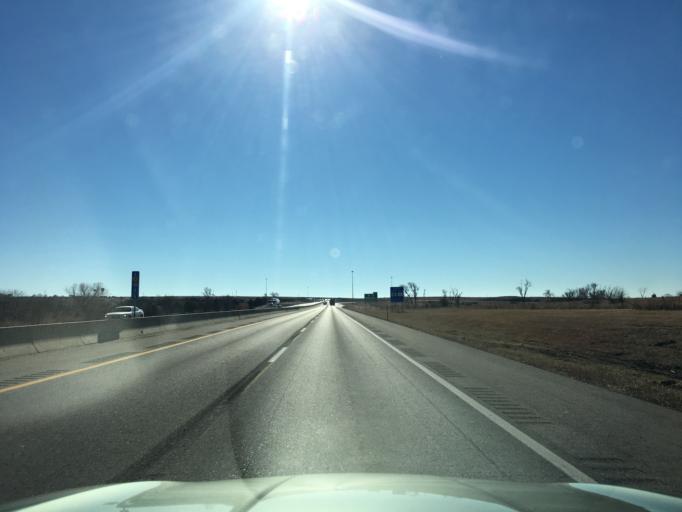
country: US
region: Kansas
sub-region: Sumner County
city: Wellington
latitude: 37.0655
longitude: -97.3385
